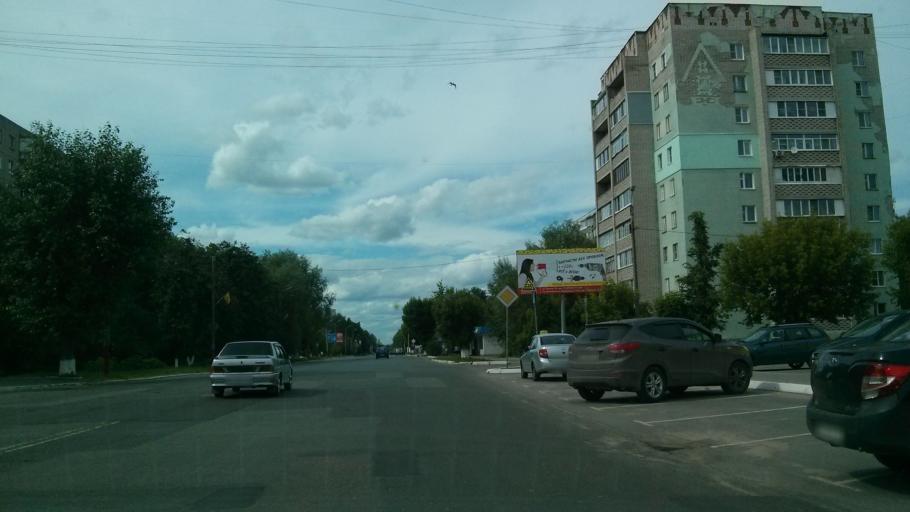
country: RU
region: Vladimir
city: Murom
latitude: 55.5676
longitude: 42.0609
